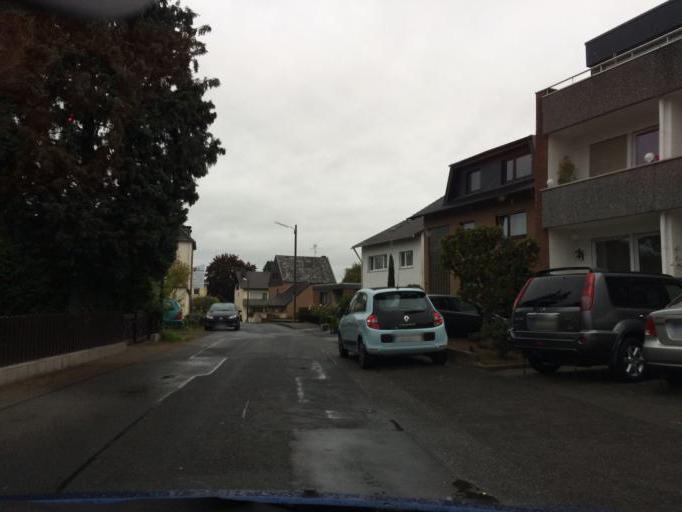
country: DE
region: North Rhine-Westphalia
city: Bruhl
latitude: 50.7766
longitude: 6.9254
